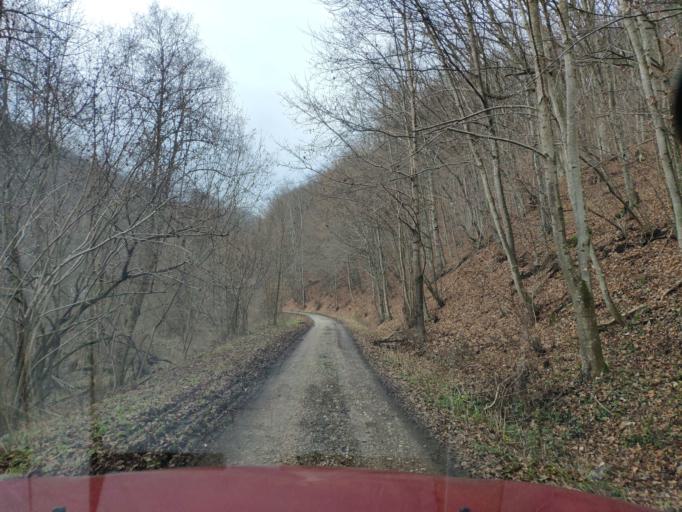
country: SK
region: Kosicky
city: Gelnica
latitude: 48.8179
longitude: 21.0577
